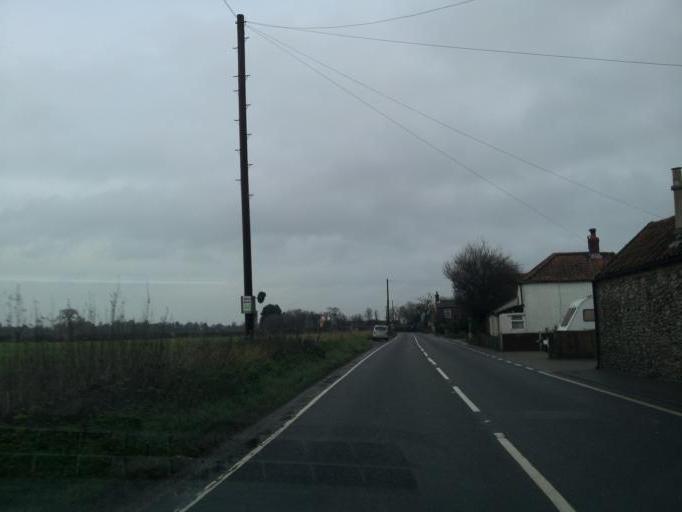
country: GB
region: England
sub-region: Norfolk
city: Acle
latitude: 52.6613
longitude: 1.5845
